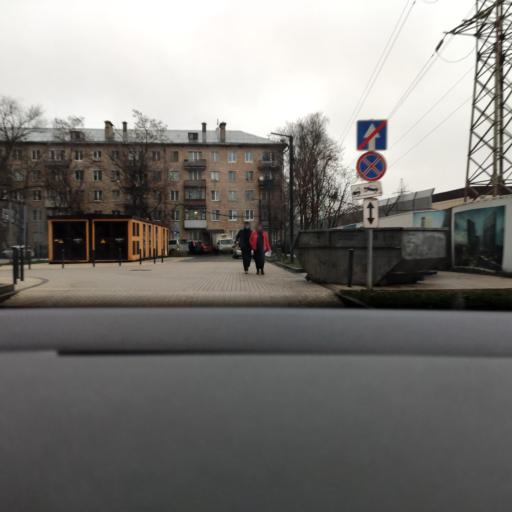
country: RU
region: Moskovskaya
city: Koptevo
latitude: 55.8100
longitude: 37.5401
